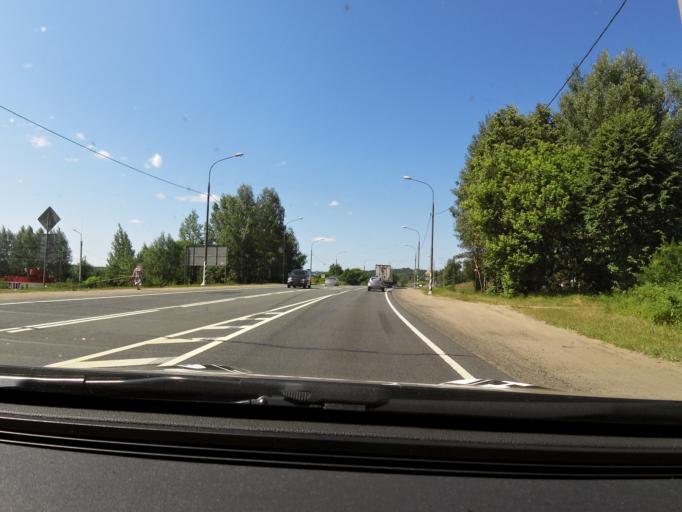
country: RU
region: Novgorod
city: Valday
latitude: 58.0319
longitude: 32.9748
